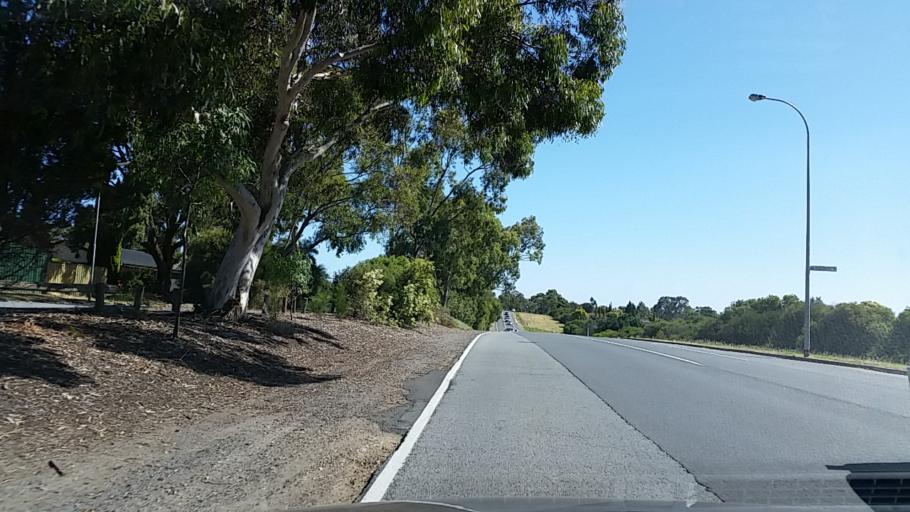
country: AU
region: South Australia
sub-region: Tea Tree Gully
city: Golden Grove
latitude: -34.7986
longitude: 138.7070
